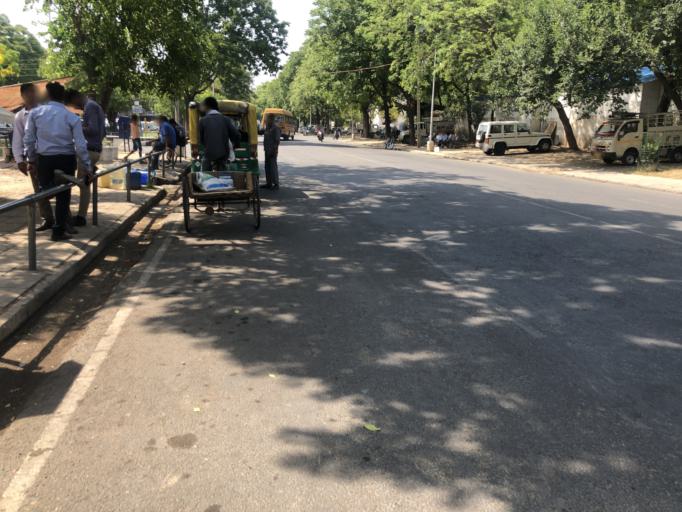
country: IN
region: Chandigarh
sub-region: Chandigarh
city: Chandigarh
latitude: 30.6943
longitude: 76.7713
